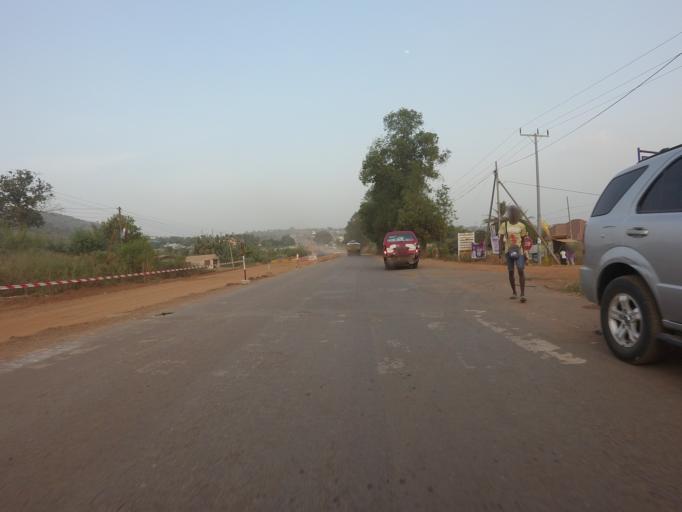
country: GH
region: Volta
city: Ho
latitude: 6.5944
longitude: 0.4396
